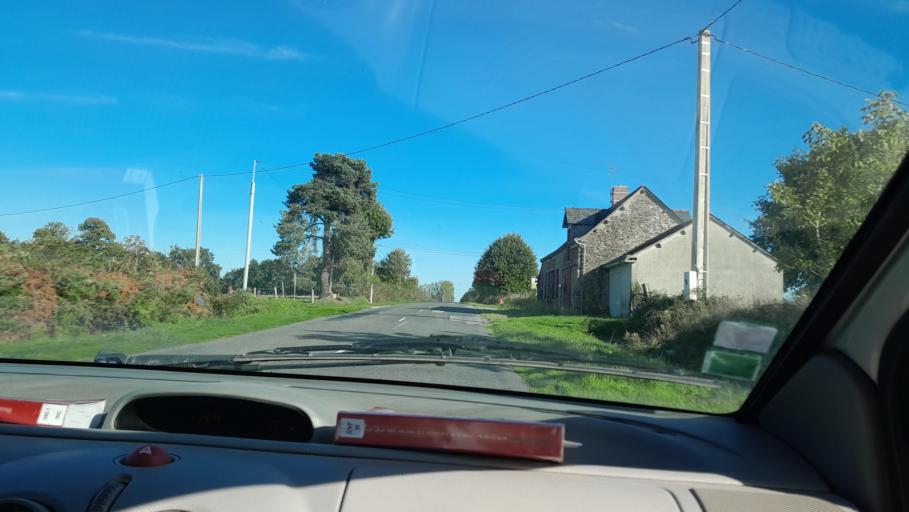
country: FR
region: Brittany
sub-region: Departement d'Ille-et-Vilaine
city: Le Pertre
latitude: 47.9675
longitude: -1.0723
